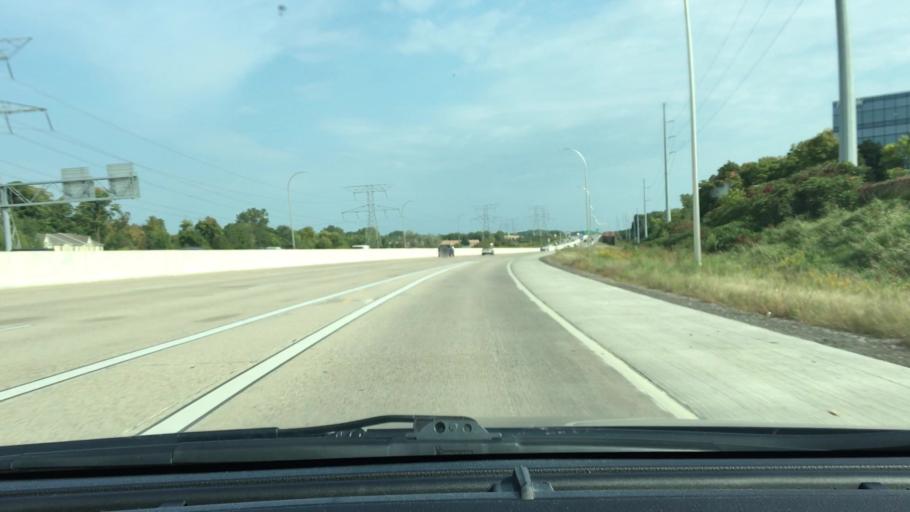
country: US
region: Minnesota
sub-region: Hennepin County
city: Plymouth
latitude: 45.0142
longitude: -93.4569
